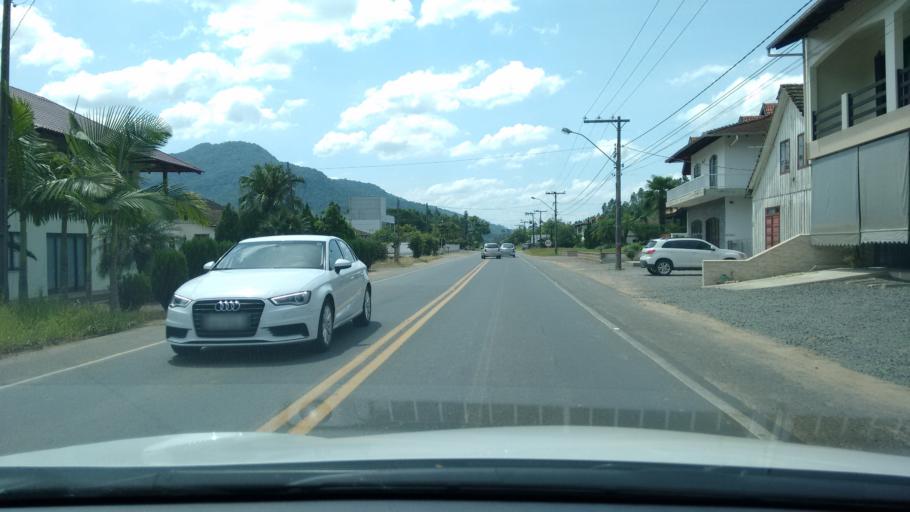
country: BR
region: Santa Catarina
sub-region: Timbo
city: Timbo
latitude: -26.8441
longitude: -49.3263
